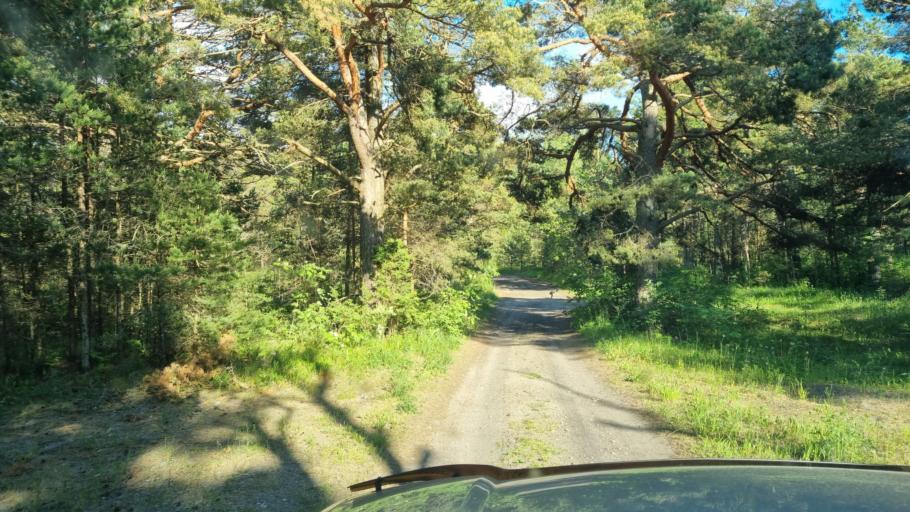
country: LV
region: Ventspils
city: Ventspils
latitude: 57.3638
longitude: 21.5105
